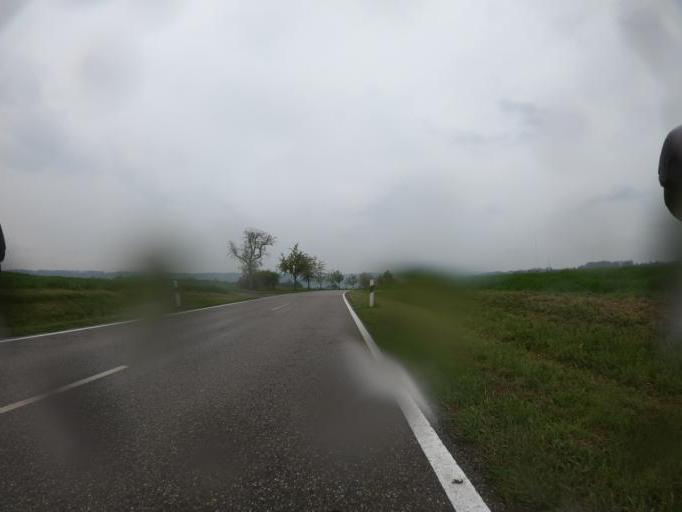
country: DE
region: Baden-Wuerttemberg
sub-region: Karlsruhe Region
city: Illingen
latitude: 48.9453
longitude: 8.8844
